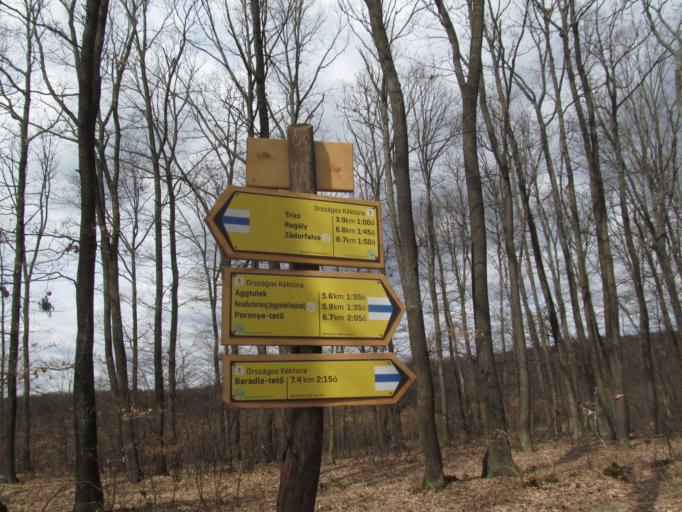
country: HU
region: Borsod-Abauj-Zemplen
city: Putnok
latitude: 48.4361
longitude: 20.4643
